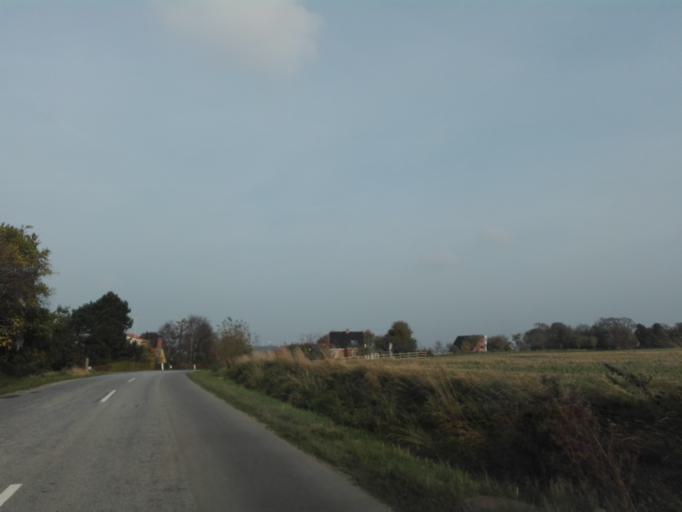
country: DK
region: Central Jutland
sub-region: Arhus Kommune
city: Solbjerg
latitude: 56.0662
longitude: 10.0964
